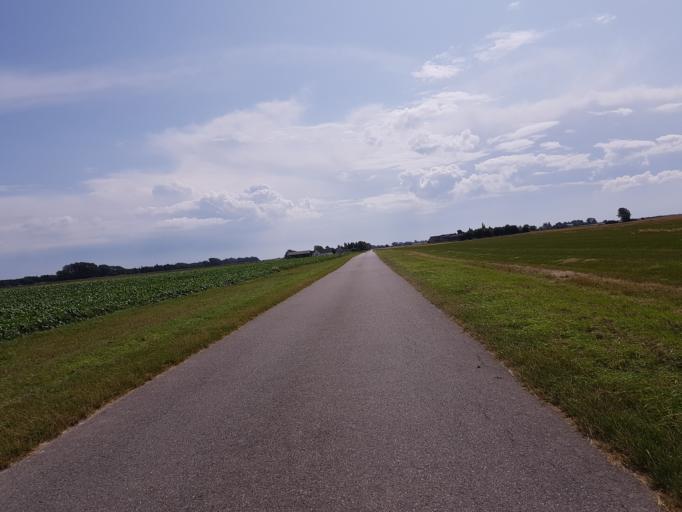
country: DK
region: Zealand
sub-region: Guldborgsund Kommune
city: Nykobing Falster
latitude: 54.5928
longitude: 11.9514
